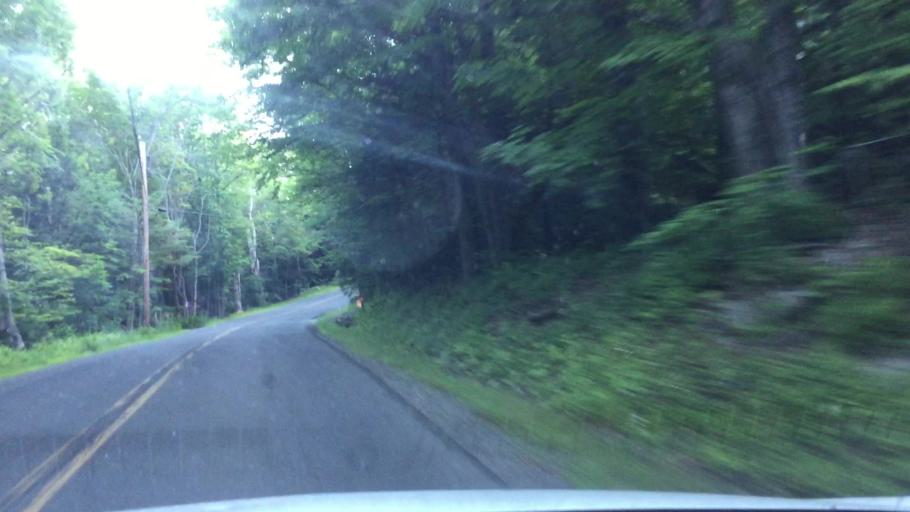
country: US
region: Massachusetts
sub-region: Berkshire County
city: Otis
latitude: 42.2424
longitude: -73.1125
